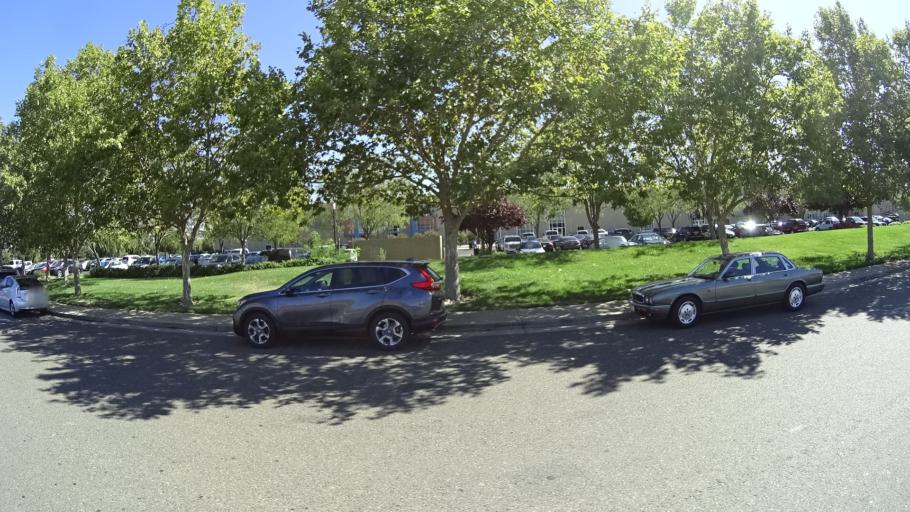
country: US
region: California
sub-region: Sacramento County
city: Laguna
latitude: 38.4289
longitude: -121.4656
